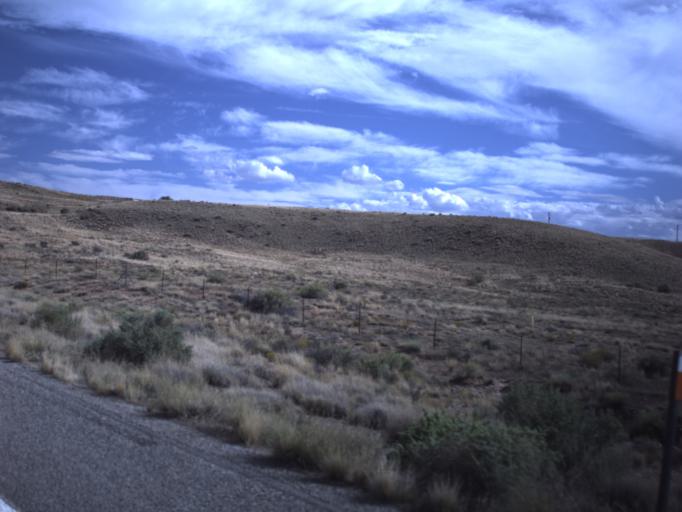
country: US
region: Colorado
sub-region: Montezuma County
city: Towaoc
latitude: 37.1953
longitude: -109.1463
